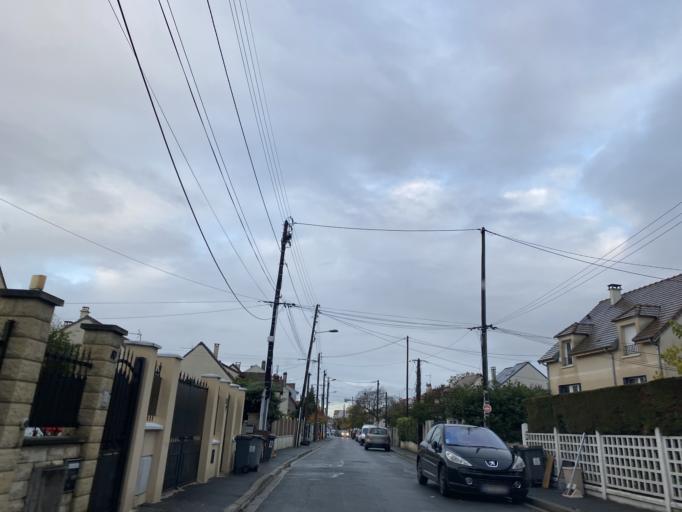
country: FR
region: Ile-de-France
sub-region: Departement des Yvelines
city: Houilles
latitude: 48.9274
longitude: 2.2018
